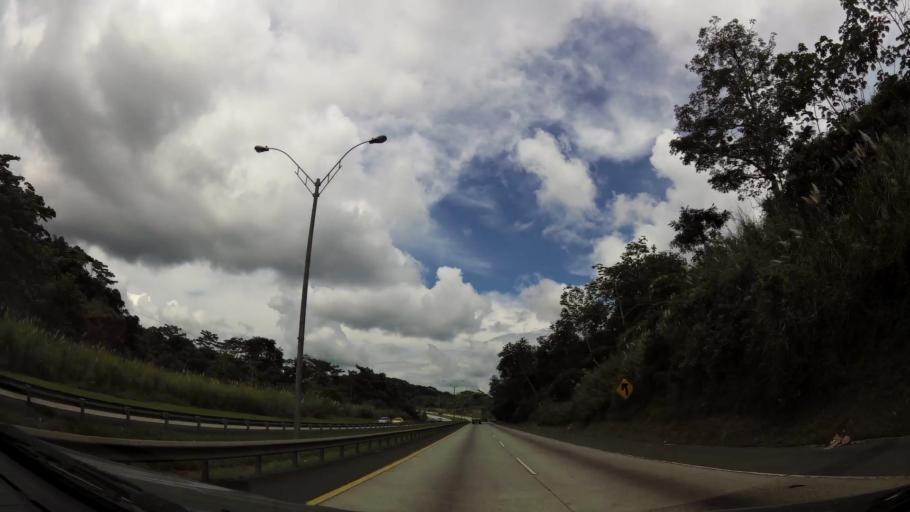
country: PA
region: Panama
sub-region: Distrito Arraijan
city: Arraijan
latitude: 8.9874
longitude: -79.6481
